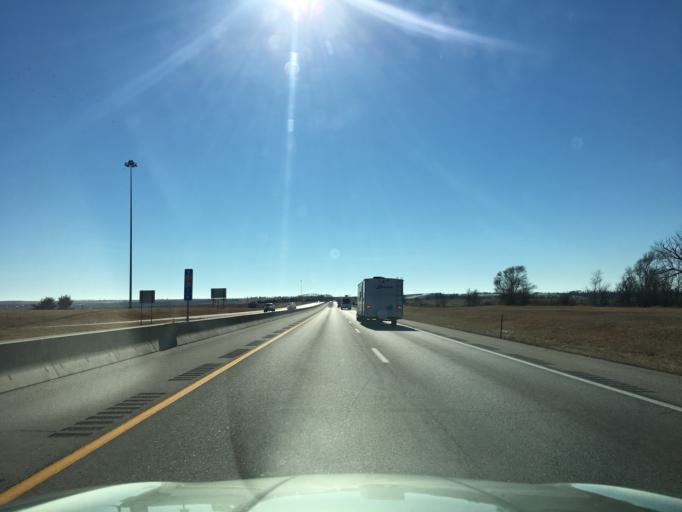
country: US
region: Oklahoma
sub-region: Kay County
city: Blackwell
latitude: 37.0222
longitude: -97.3382
